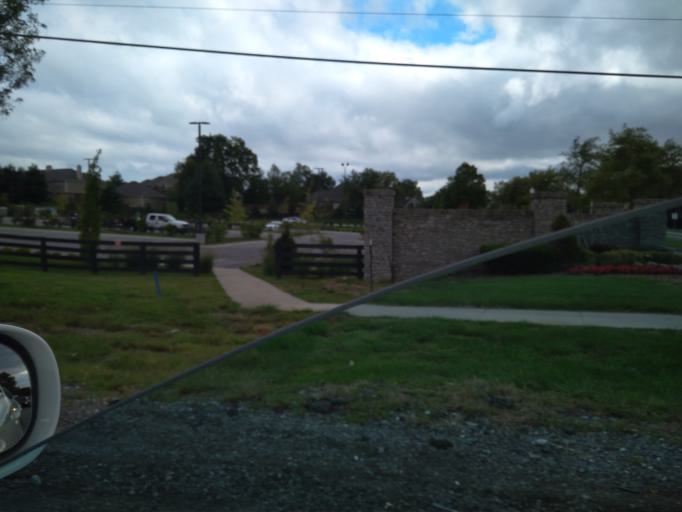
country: US
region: Kentucky
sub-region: Jefferson County
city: Worthington
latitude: 38.2962
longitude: -85.5530
